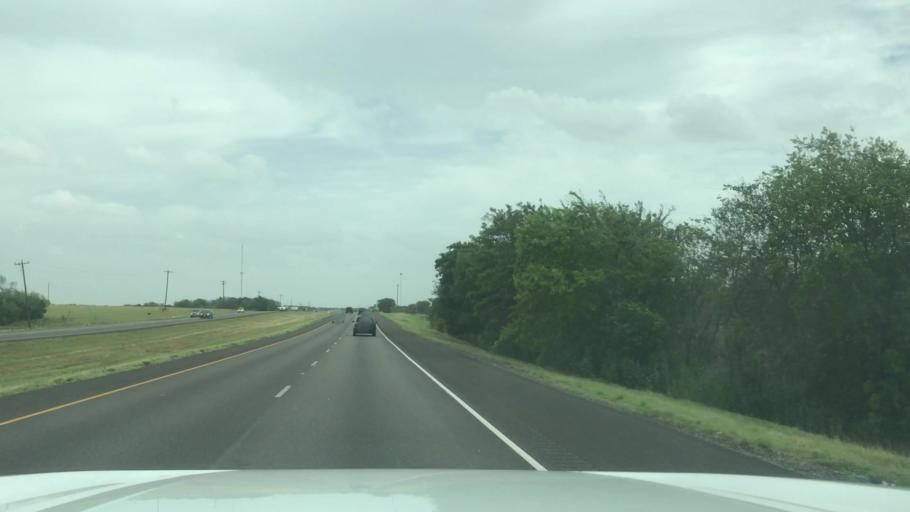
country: US
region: Texas
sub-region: McLennan County
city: Riesel
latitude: 31.5189
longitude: -96.9757
